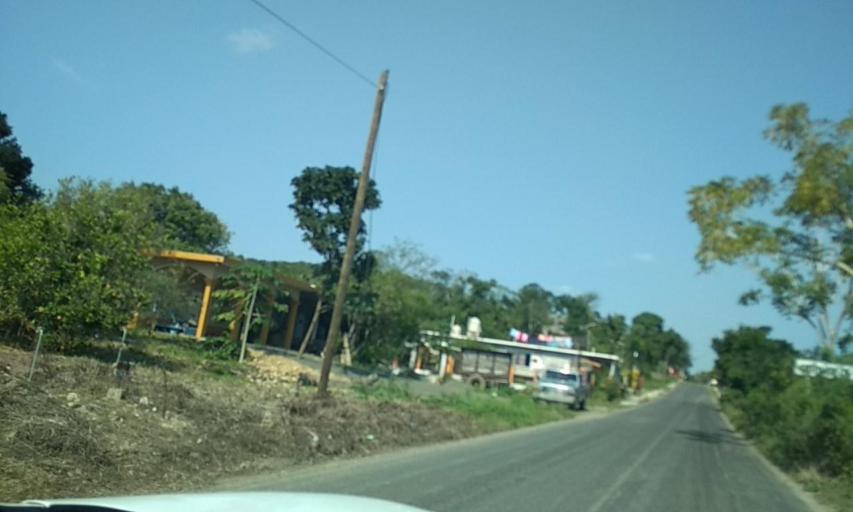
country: MX
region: Veracruz
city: Gutierrez Zamora
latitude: 20.3491
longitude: -97.1497
